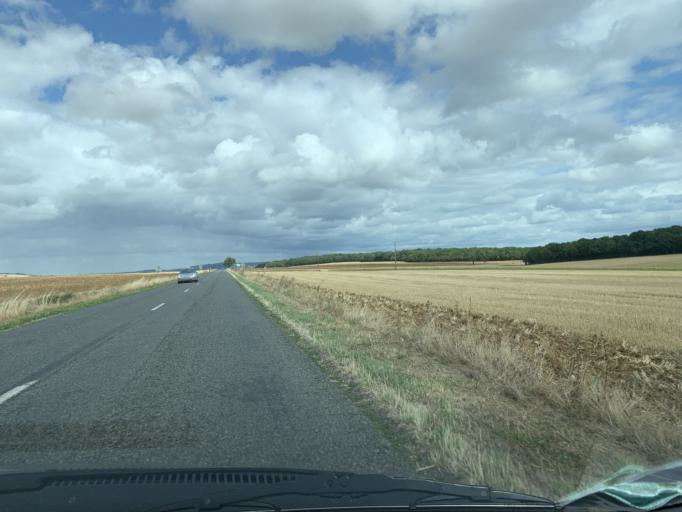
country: FR
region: Bourgogne
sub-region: Departement de la Nievre
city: Clamecy
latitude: 47.4190
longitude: 3.4642
